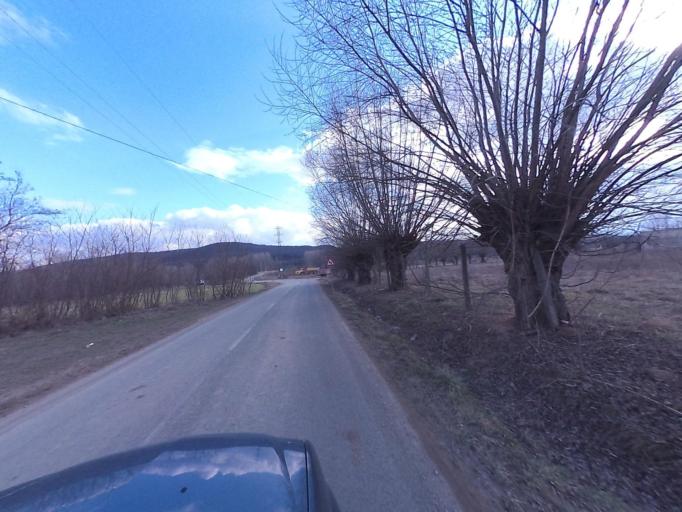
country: RO
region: Neamt
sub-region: Oras Targu Neamt
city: Targu Neamt
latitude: 47.2011
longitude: 26.4050
